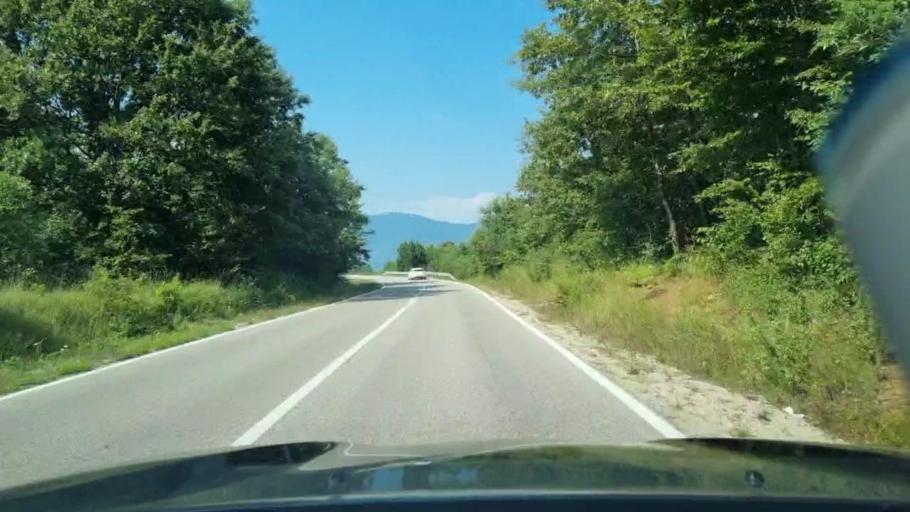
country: BA
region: Federation of Bosnia and Herzegovina
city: Ostrozac
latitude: 44.8708
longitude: 15.8992
